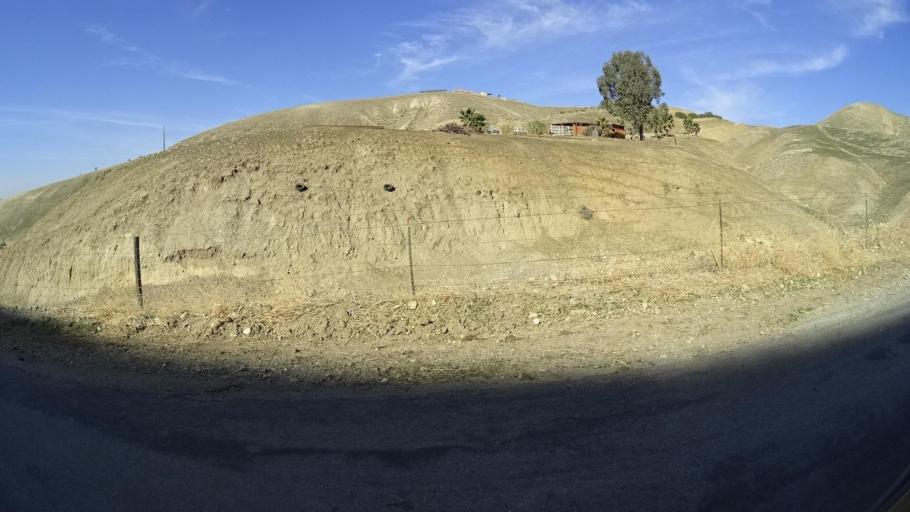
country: US
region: California
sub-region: Kern County
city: Lamont
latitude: 35.4011
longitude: -118.7972
